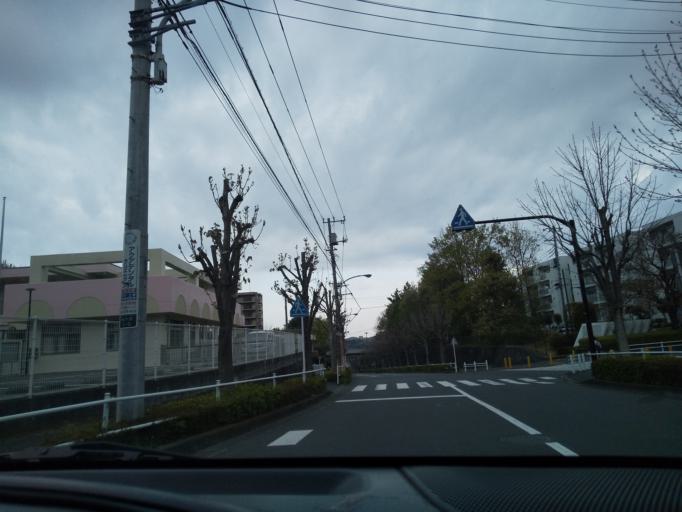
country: JP
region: Tokyo
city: Hino
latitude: 35.6081
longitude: 139.3822
